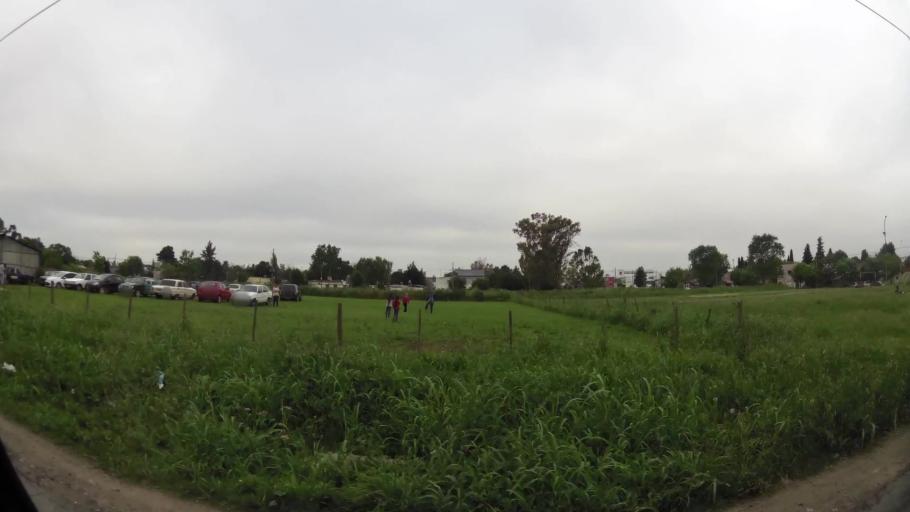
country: AR
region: Buenos Aires
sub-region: Partido de La Plata
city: La Plata
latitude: -34.9282
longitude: -57.9922
